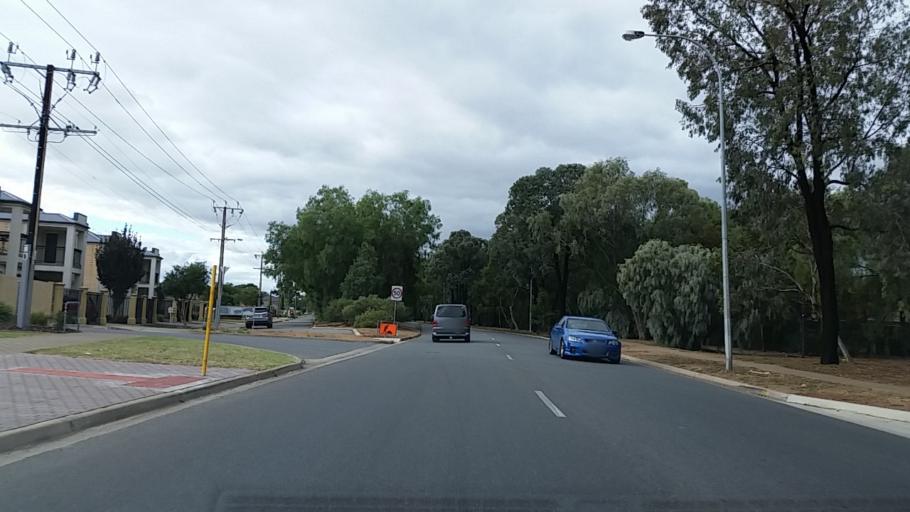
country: AU
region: South Australia
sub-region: Salisbury
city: Salisbury
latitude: -34.7810
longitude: 138.6089
